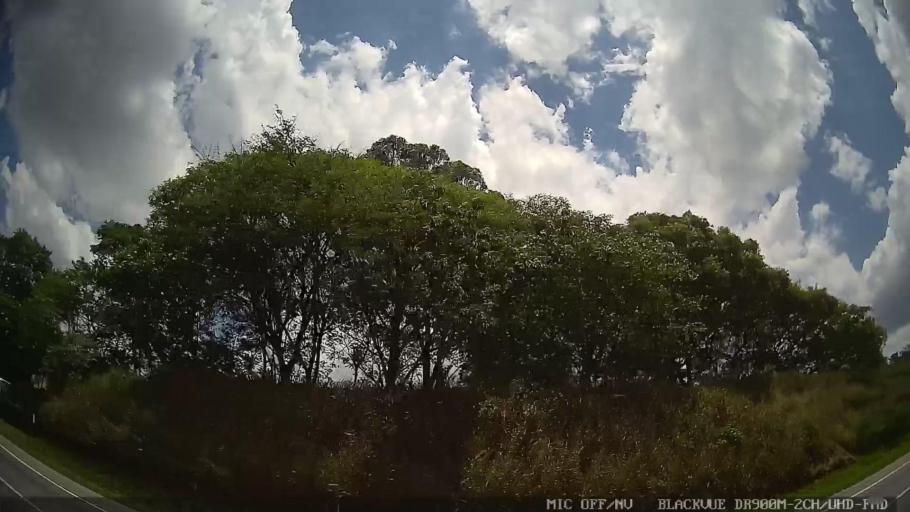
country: BR
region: Sao Paulo
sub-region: Osasco
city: Osasco
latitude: -23.4612
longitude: -46.7528
